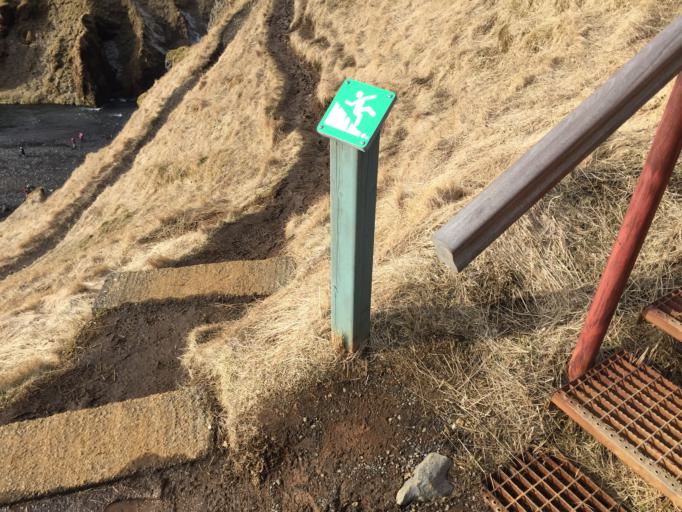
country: IS
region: South
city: Vestmannaeyjar
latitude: 63.5313
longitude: -19.5103
